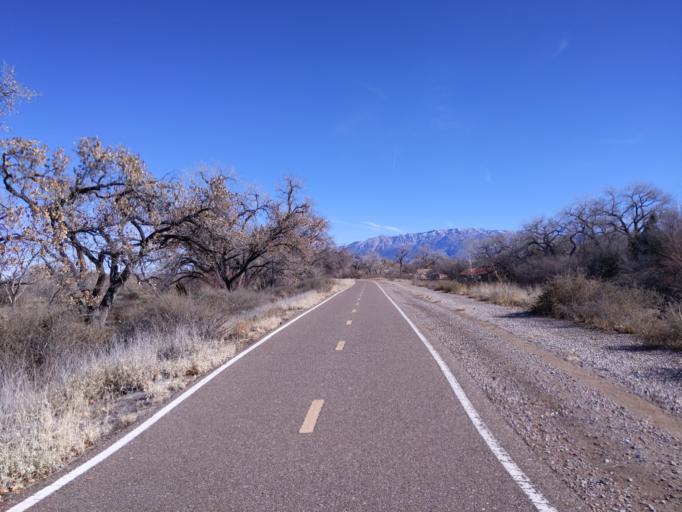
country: US
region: New Mexico
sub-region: Bernalillo County
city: Los Ranchos de Albuquerque
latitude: 35.1624
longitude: -106.6622
